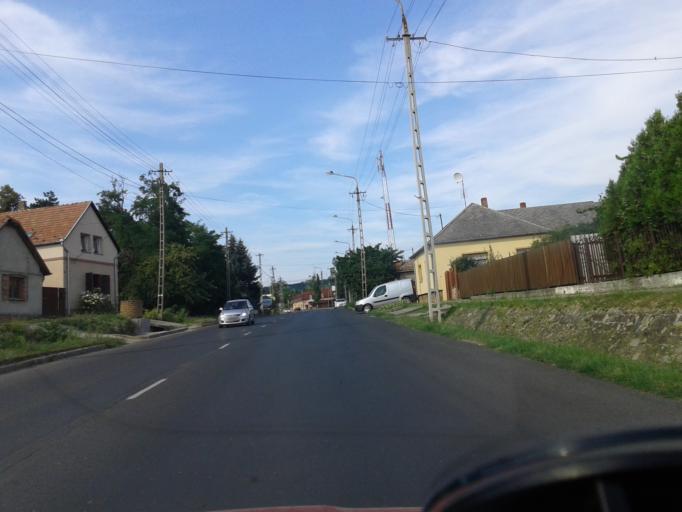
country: HU
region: Pest
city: Kerepes
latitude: 47.5662
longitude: 19.2916
